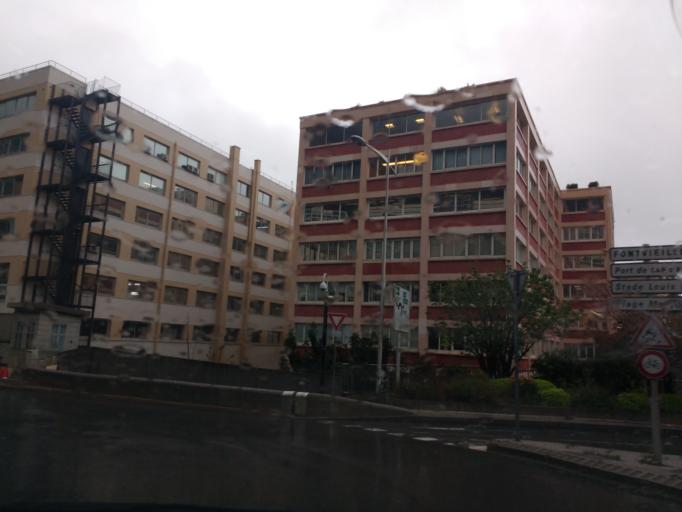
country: MC
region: Commune de Monaco
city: Fontvieille
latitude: 43.7280
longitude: 7.4122
